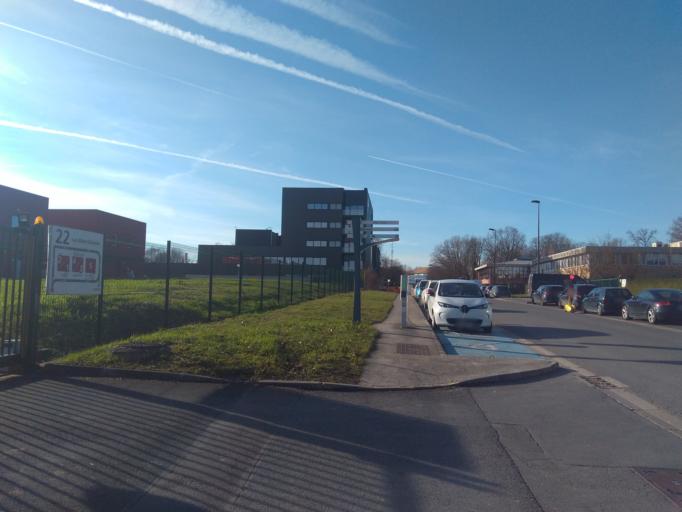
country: FR
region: Ile-de-France
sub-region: Departement de Seine-et-Marne
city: Champs-sur-Marne
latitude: 48.8351
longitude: 2.5898
